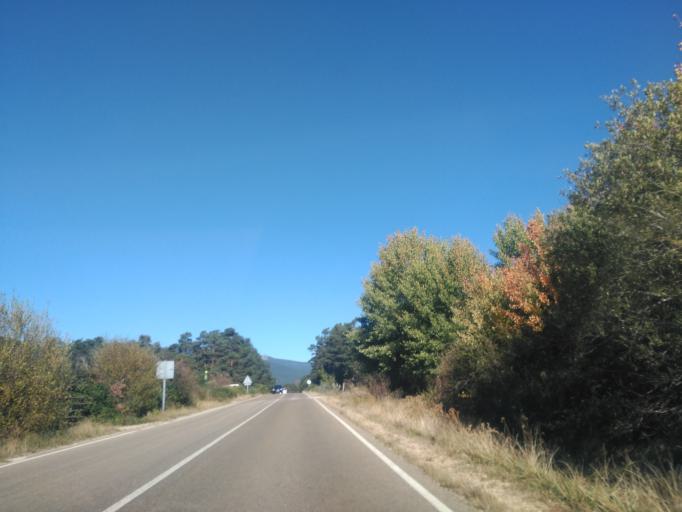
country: ES
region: Castille and Leon
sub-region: Provincia de Soria
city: Vinuesa
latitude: 41.9167
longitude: -2.7553
